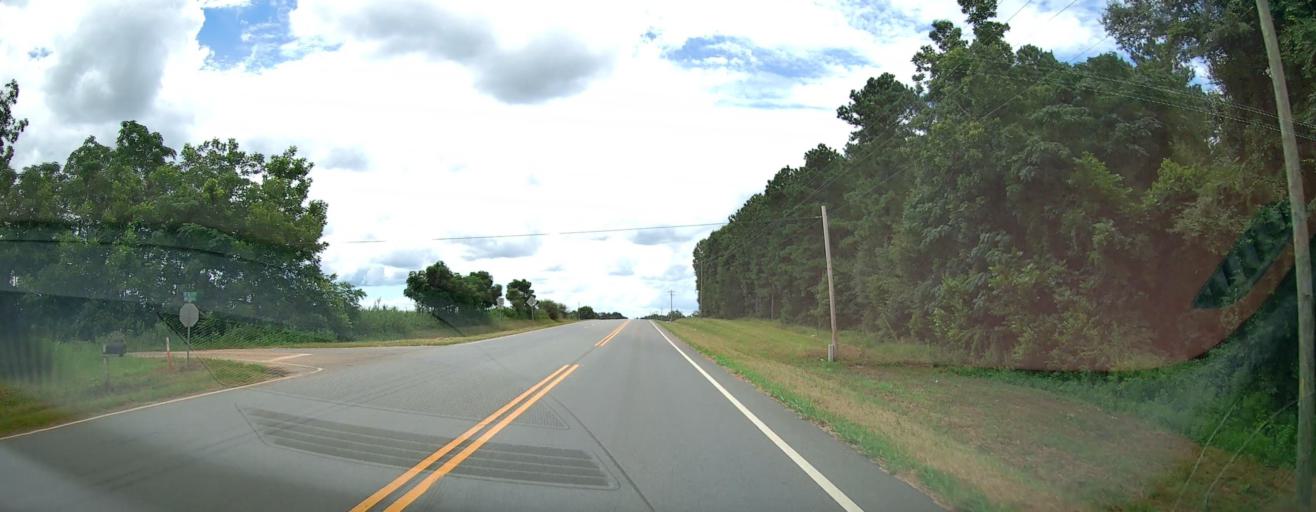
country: US
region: Georgia
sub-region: Macon County
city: Montezuma
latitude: 32.2918
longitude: -83.9272
